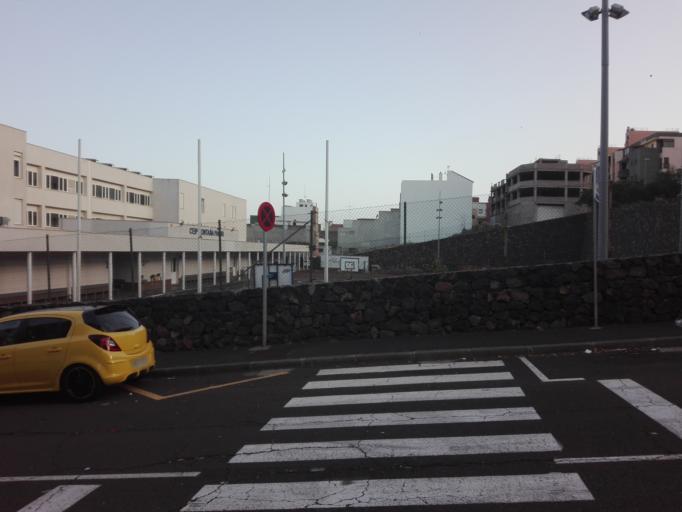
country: ES
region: Canary Islands
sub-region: Provincia de Santa Cruz de Tenerife
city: La Laguna
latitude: 28.4564
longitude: -16.3017
